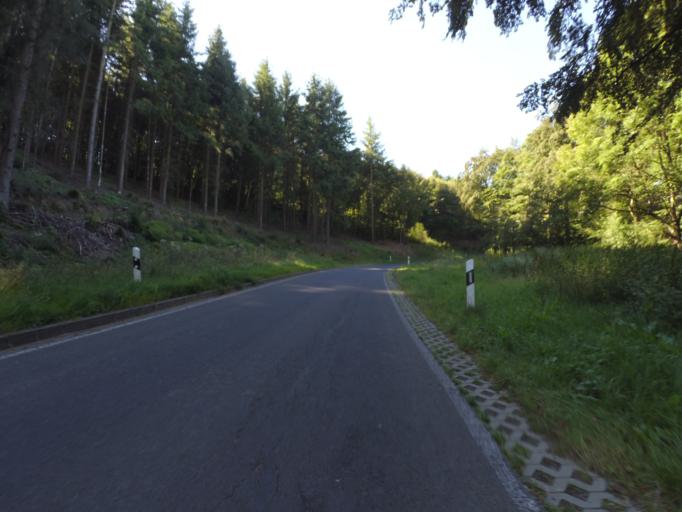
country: DE
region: Rheinland-Pfalz
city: Niederstadtfeld
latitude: 50.1698
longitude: 6.7776
